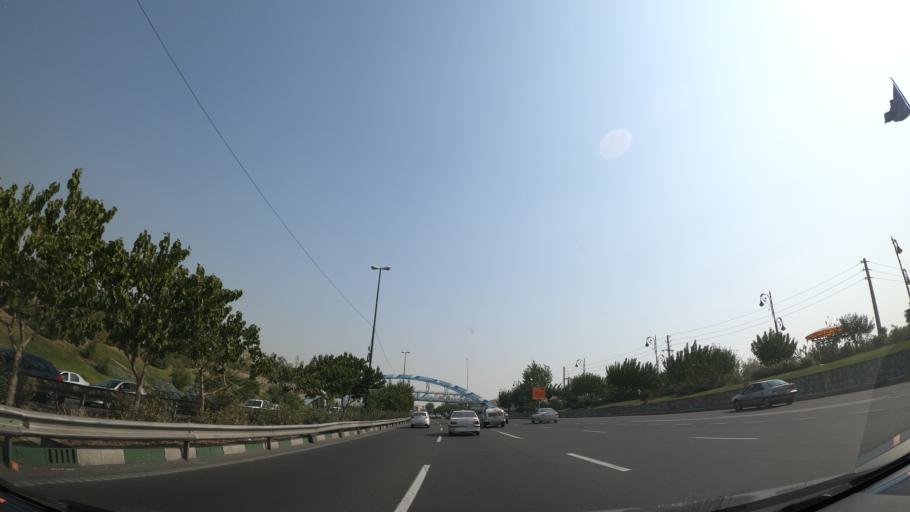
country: IR
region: Tehran
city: Tehran
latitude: 35.7545
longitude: 51.2716
